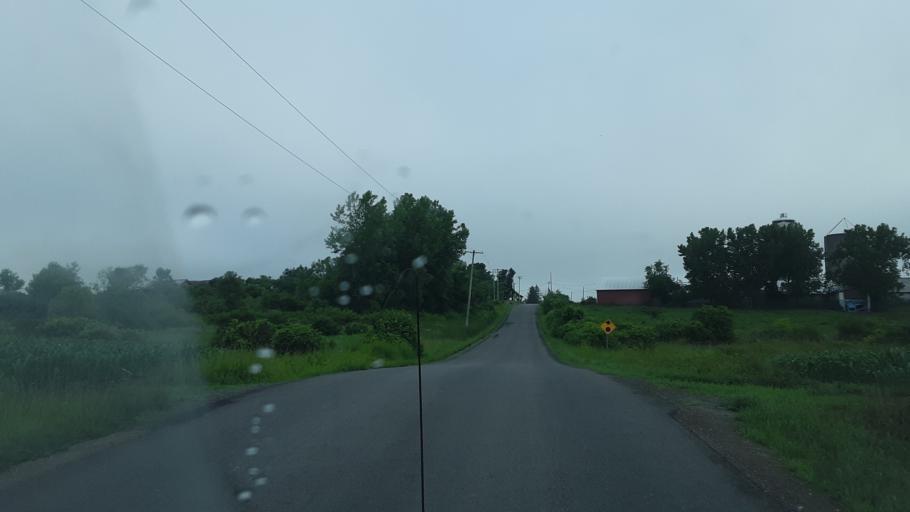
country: US
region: New York
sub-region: Montgomery County
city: Fonda
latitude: 42.8924
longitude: -74.3817
